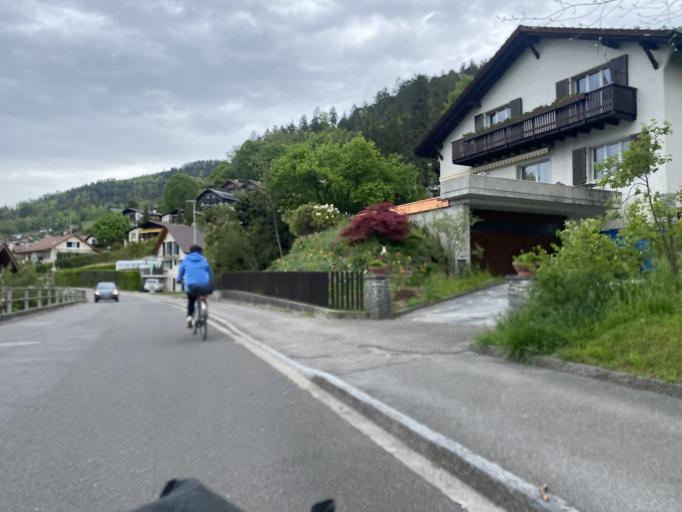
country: CH
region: Bern
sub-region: Thun District
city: Hilterfingen
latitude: 46.7431
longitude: 7.6535
